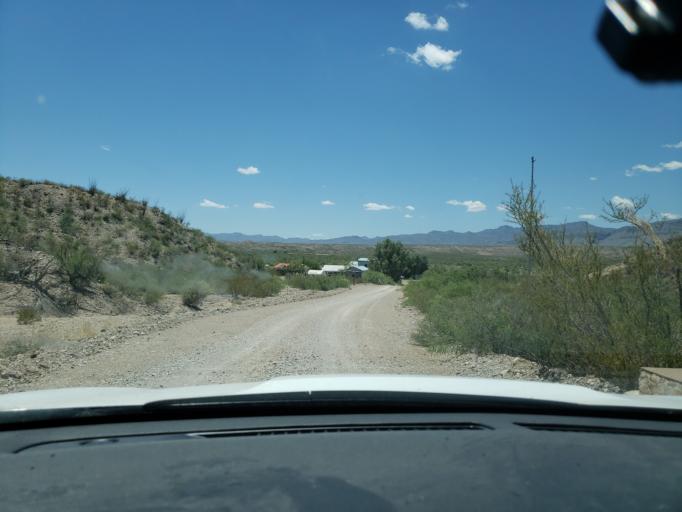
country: MX
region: Chihuahua
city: Ojinaga
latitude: 29.9841
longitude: -104.6789
